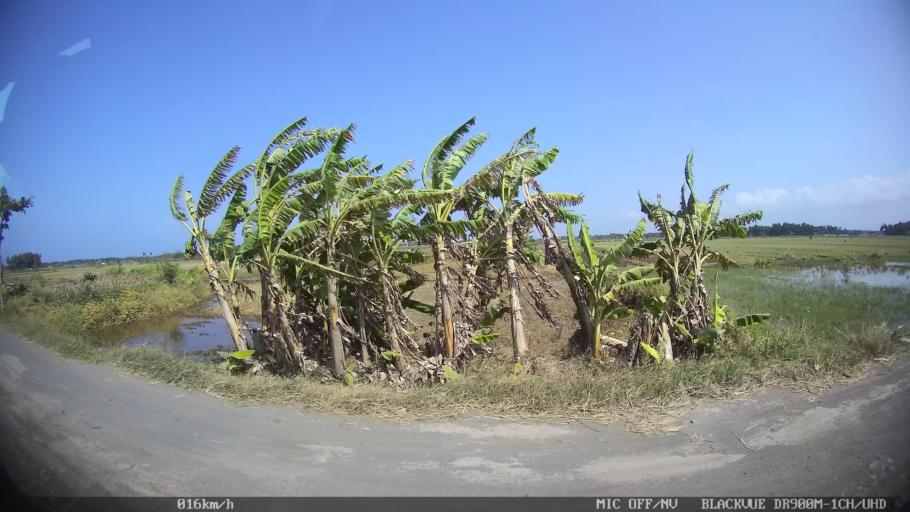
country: ID
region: Daerah Istimewa Yogyakarta
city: Srandakan
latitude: -7.9695
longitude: 110.2116
